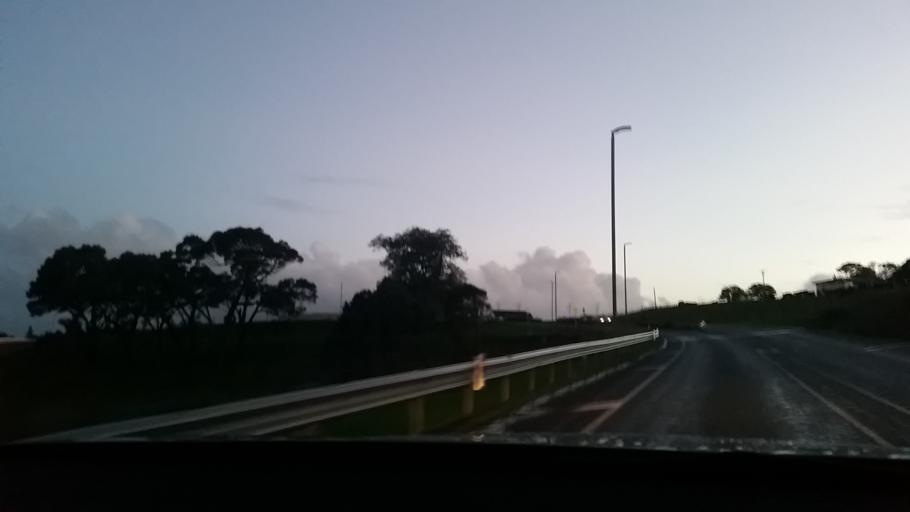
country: NZ
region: Waikato
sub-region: Hamilton City
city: Hamilton
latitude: -37.8168
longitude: 175.2279
